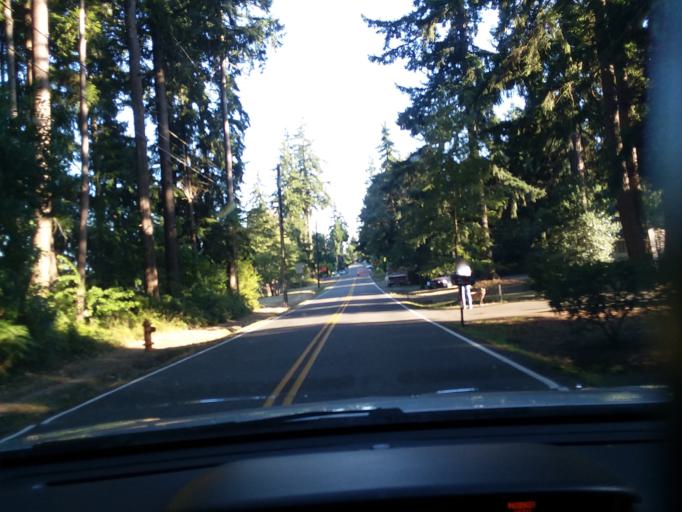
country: US
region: Washington
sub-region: Snohomish County
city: Esperance
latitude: 47.7973
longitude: -122.3411
